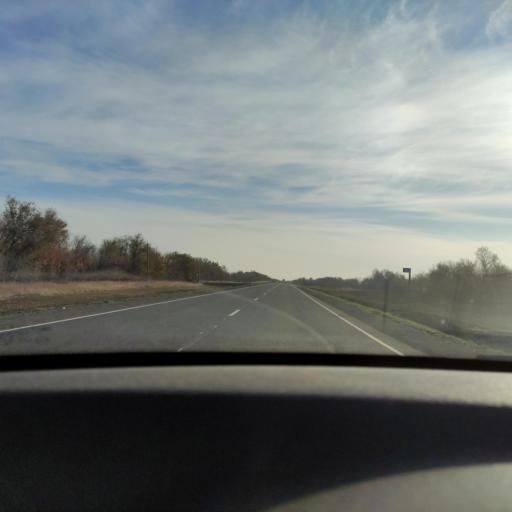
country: RU
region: Samara
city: Krasnoarmeyskoye
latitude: 52.8313
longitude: 50.0067
